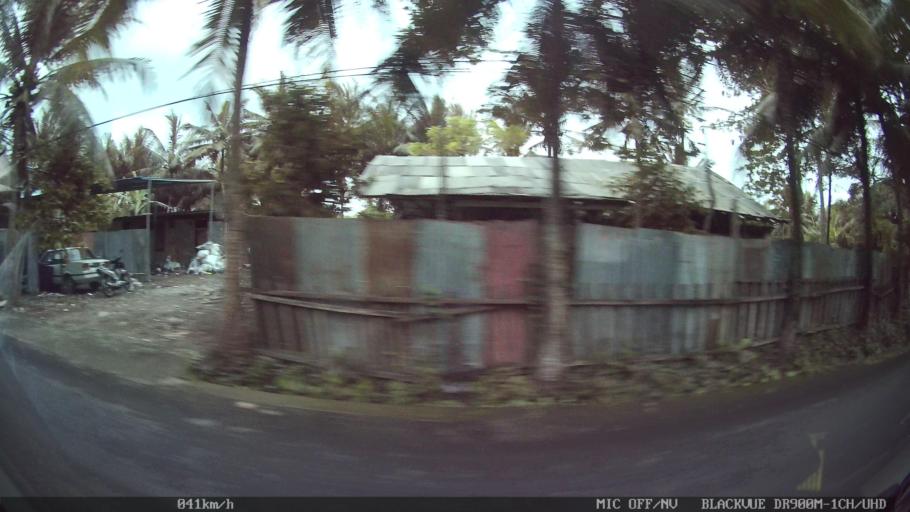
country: ID
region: Bali
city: Banjar Cemenggon
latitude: -8.5420
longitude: 115.2093
